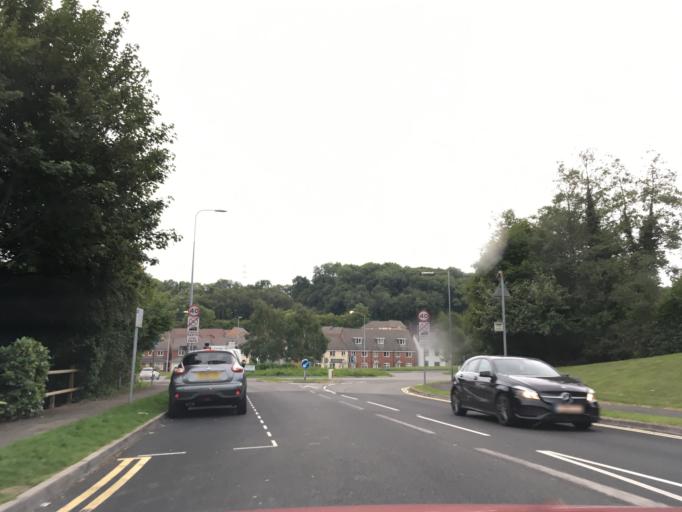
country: GB
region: Wales
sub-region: Newport
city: Langstone
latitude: 51.6044
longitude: -2.9202
